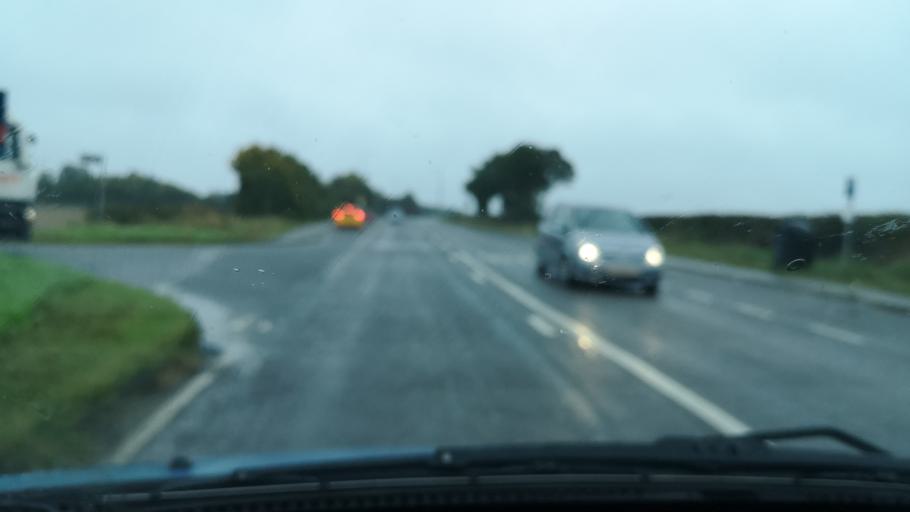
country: GB
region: England
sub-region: City and Borough of Wakefield
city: Hemsworth
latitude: 53.6293
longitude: -1.3365
